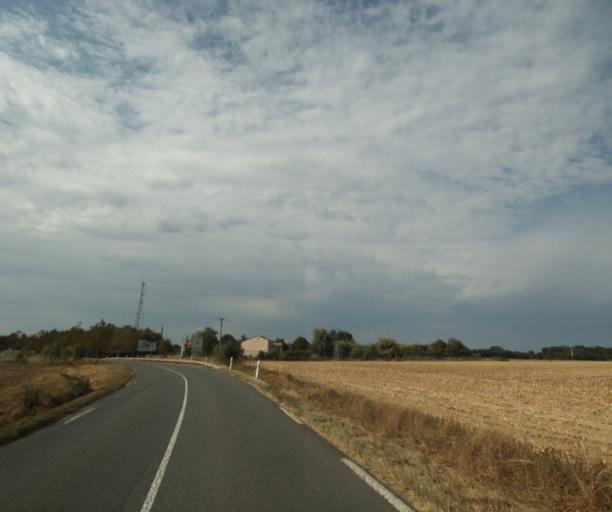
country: FR
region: Poitou-Charentes
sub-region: Departement de la Charente-Maritime
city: Cabariot
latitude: 45.9592
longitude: -0.8586
